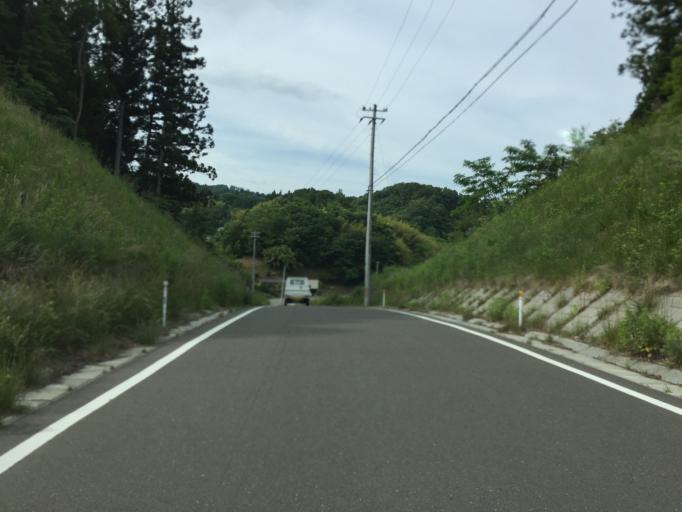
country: JP
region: Fukushima
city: Funehikimachi-funehiki
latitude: 37.4447
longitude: 140.6388
